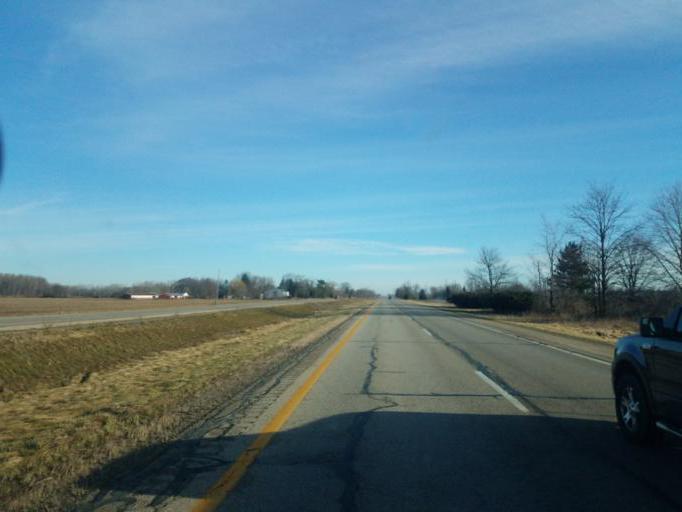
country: US
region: Michigan
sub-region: Gratiot County
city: Ithaca
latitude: 43.1972
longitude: -84.5634
